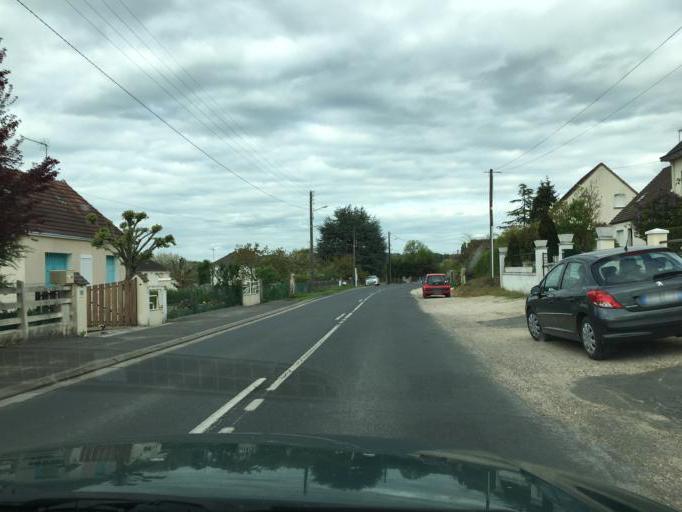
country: FR
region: Centre
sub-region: Departement du Loir-et-Cher
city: Saint-Ouen
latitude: 47.7945
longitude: 1.0939
